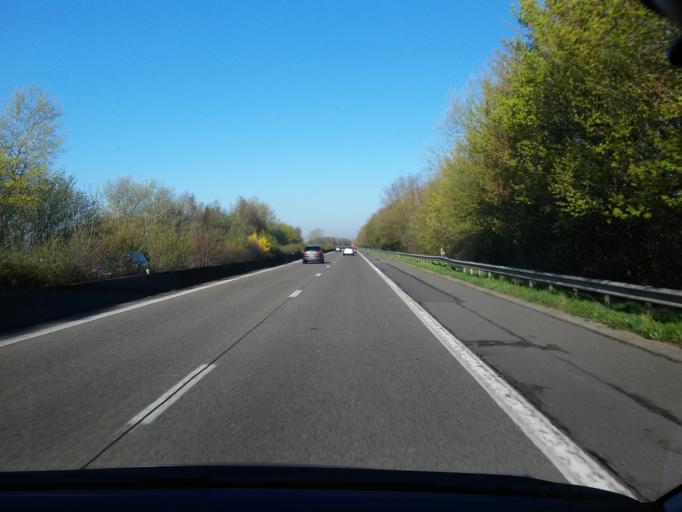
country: BE
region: Wallonia
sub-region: Province du Brabant Wallon
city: Genappe
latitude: 50.6185
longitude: 4.4887
